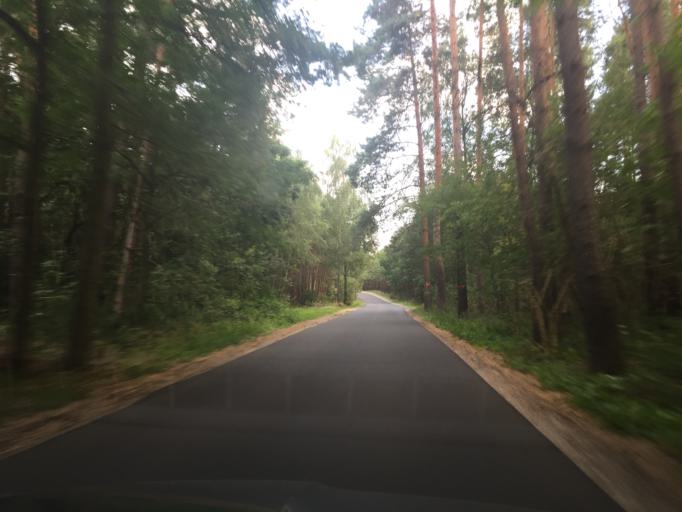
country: DE
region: Brandenburg
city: Grunheide
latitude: 52.3636
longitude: 13.7882
